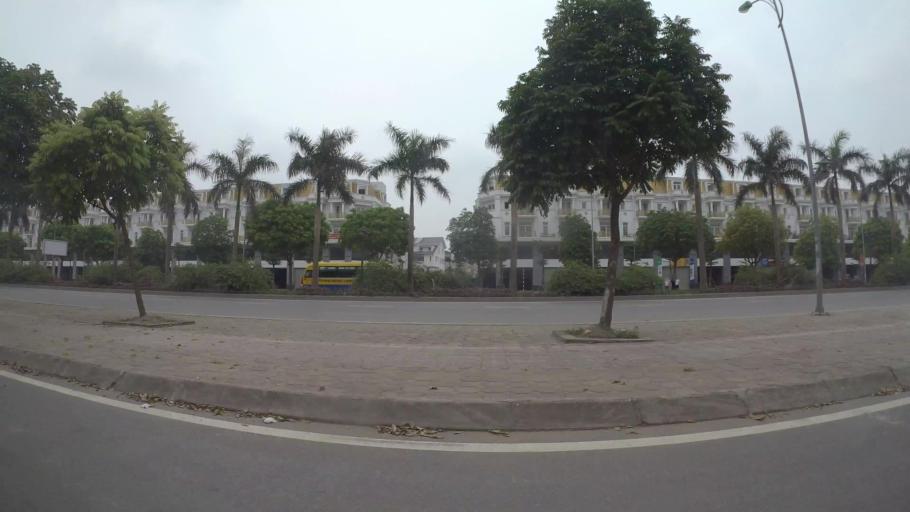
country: VN
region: Ha Noi
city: Ha Dong
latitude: 20.9853
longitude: 105.7400
